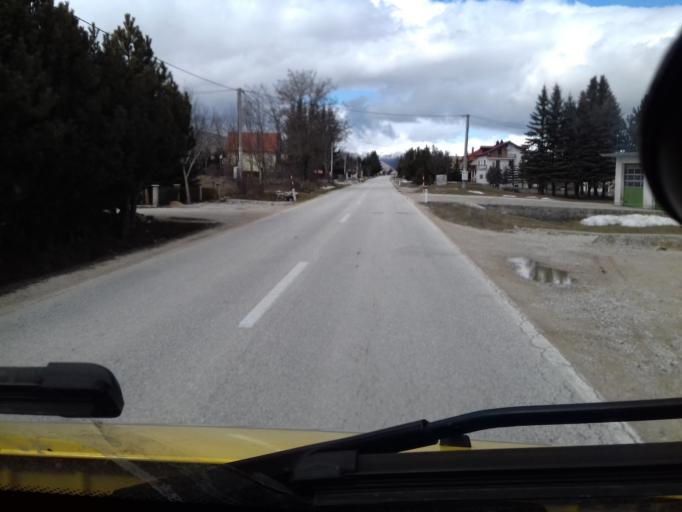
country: BA
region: Federation of Bosnia and Herzegovina
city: Tomislavgrad
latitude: 43.6263
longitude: 17.2524
